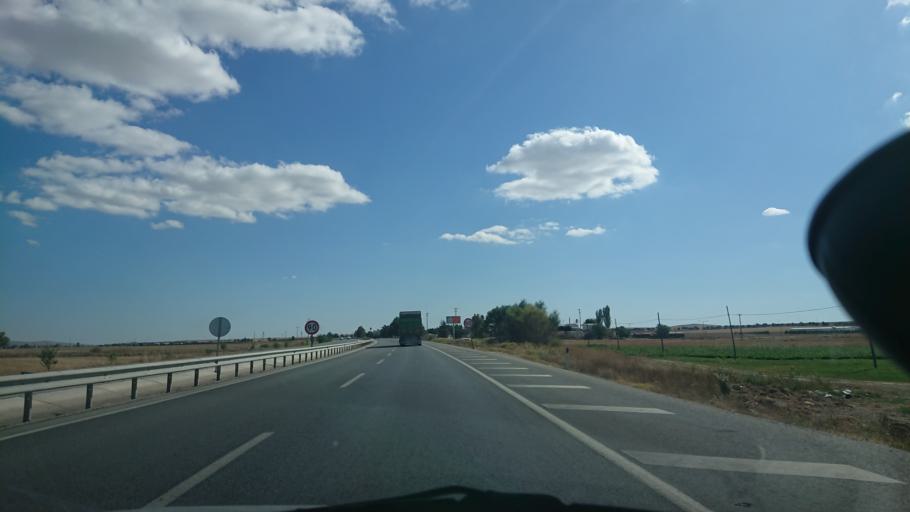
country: TR
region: Eskisehir
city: Mahmudiye
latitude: 39.5651
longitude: 30.9146
